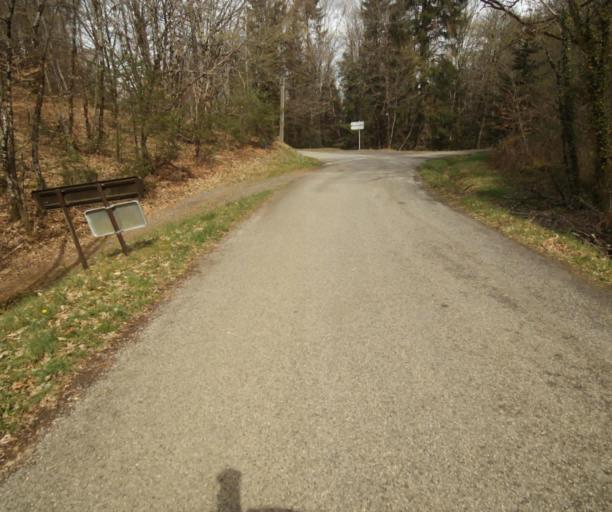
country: FR
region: Limousin
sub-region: Departement de la Correze
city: Laguenne
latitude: 45.2100
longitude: 1.8633
